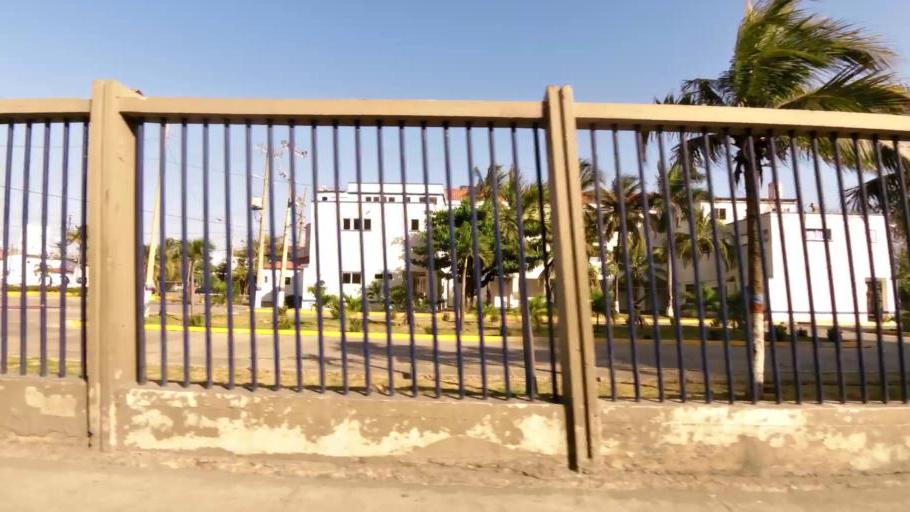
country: CO
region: Bolivar
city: Cartagena
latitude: 10.4082
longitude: -75.5509
